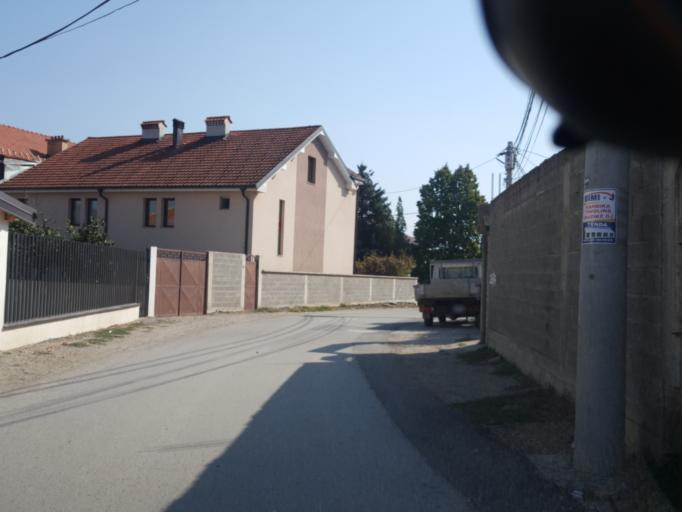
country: XK
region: Gjakova
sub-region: Komuna e Gjakoves
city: Gjakove
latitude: 42.3894
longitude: 20.4219
